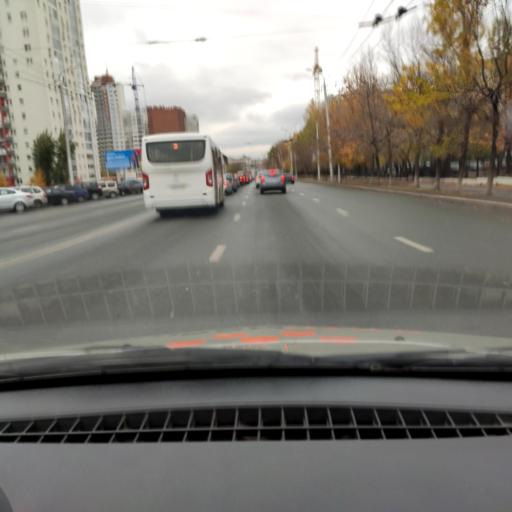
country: RU
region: Bashkortostan
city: Ufa
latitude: 54.7099
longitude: 56.0008
